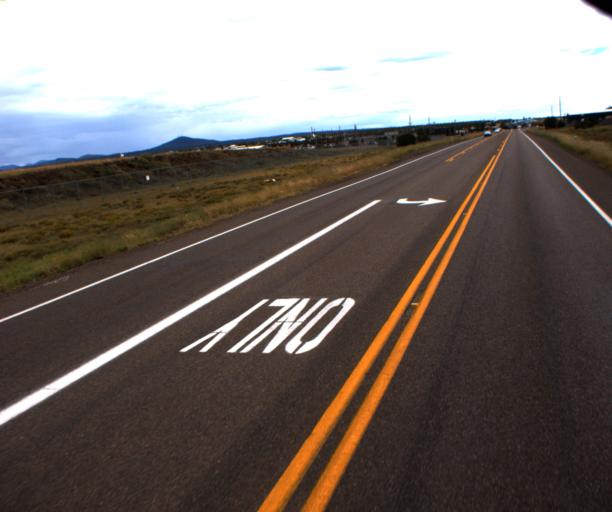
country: US
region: Arizona
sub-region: Navajo County
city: Show Low
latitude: 34.2641
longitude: -110.0208
